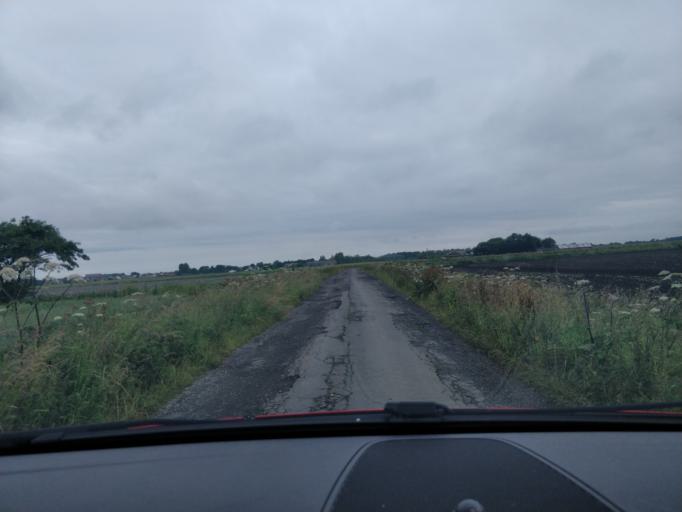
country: GB
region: England
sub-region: Lancashire
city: Banks
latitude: 53.6630
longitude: -2.9346
